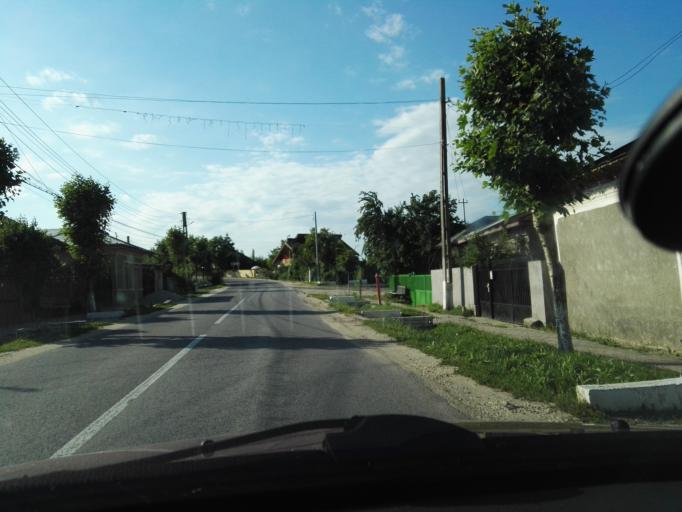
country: RO
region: Giurgiu
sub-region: Comuna Comana
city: Gradistea
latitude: 44.2219
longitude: 26.1541
